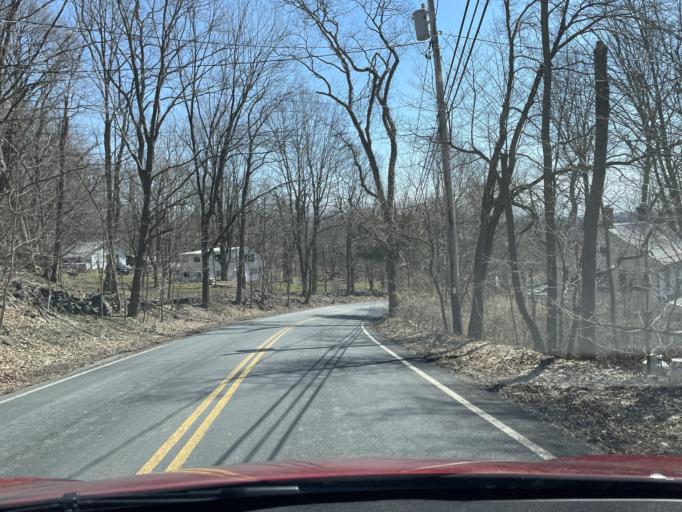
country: US
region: New York
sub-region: Ulster County
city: West Hurley
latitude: 42.0064
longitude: -74.1460
